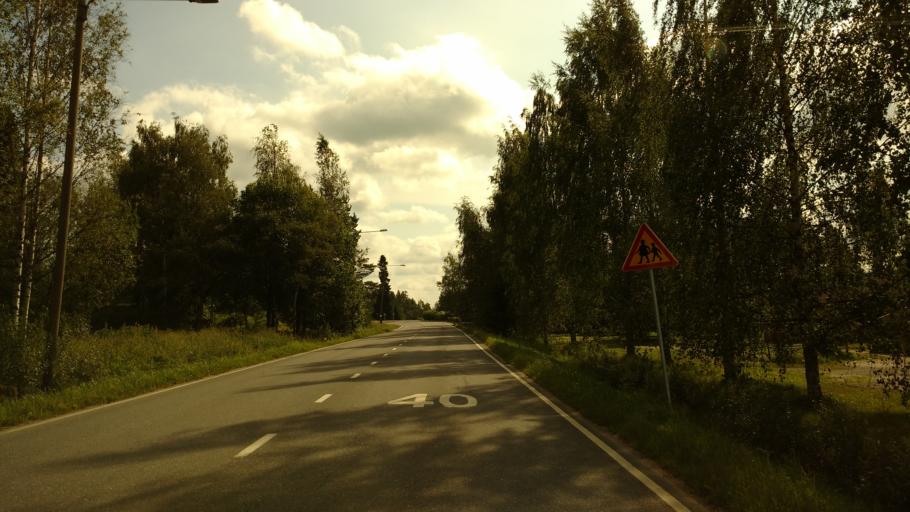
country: FI
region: Varsinais-Suomi
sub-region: Loimaa
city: Koski Tl
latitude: 60.6500
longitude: 23.1308
